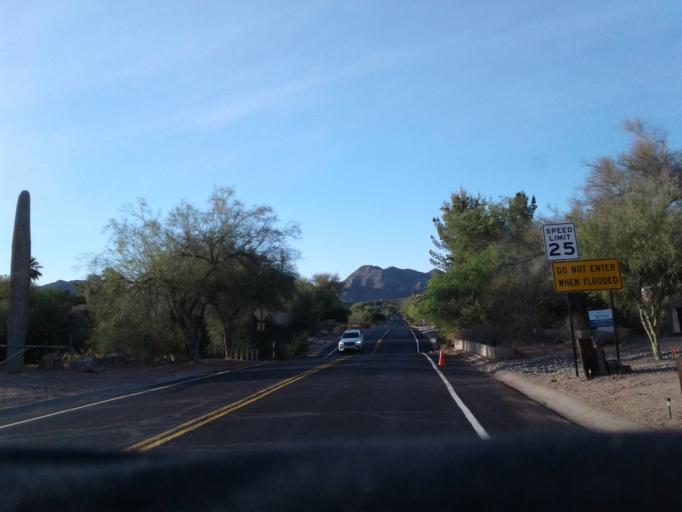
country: US
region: Arizona
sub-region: Maricopa County
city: Paradise Valley
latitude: 33.5174
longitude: -111.9952
